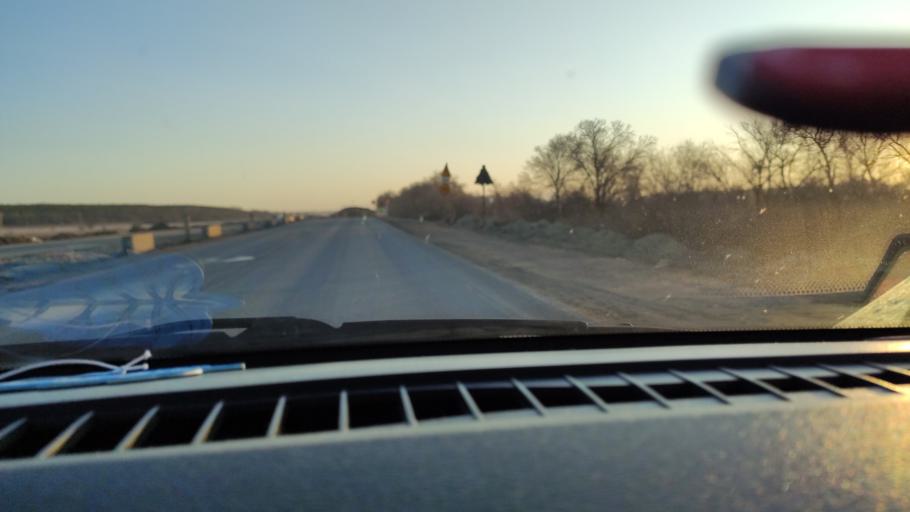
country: RU
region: Saratov
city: Sinodskoye
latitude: 52.0020
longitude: 46.6797
